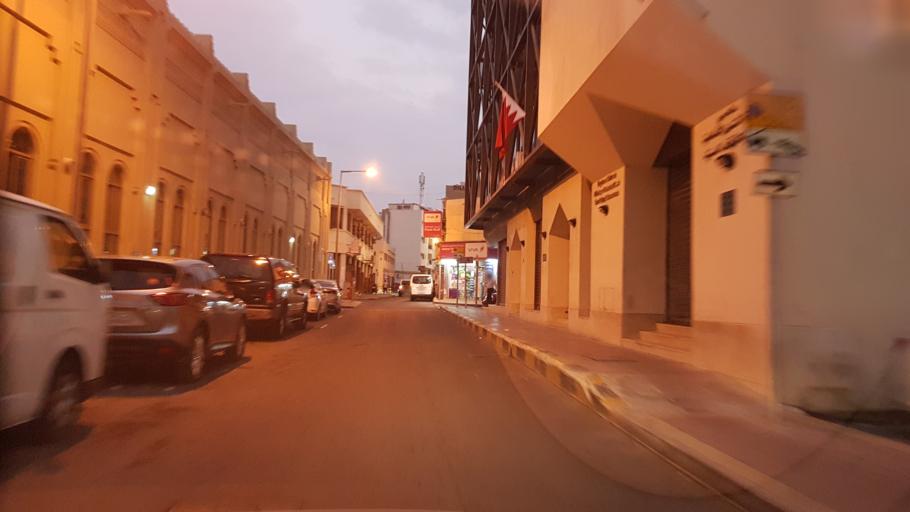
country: BH
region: Manama
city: Manama
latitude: 26.2357
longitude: 50.5794
